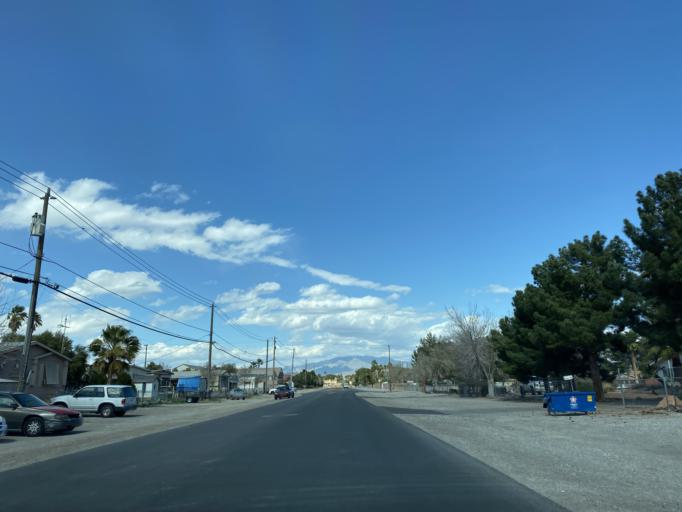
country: US
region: Nevada
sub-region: Clark County
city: Spring Valley
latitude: 36.2503
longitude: -115.2604
